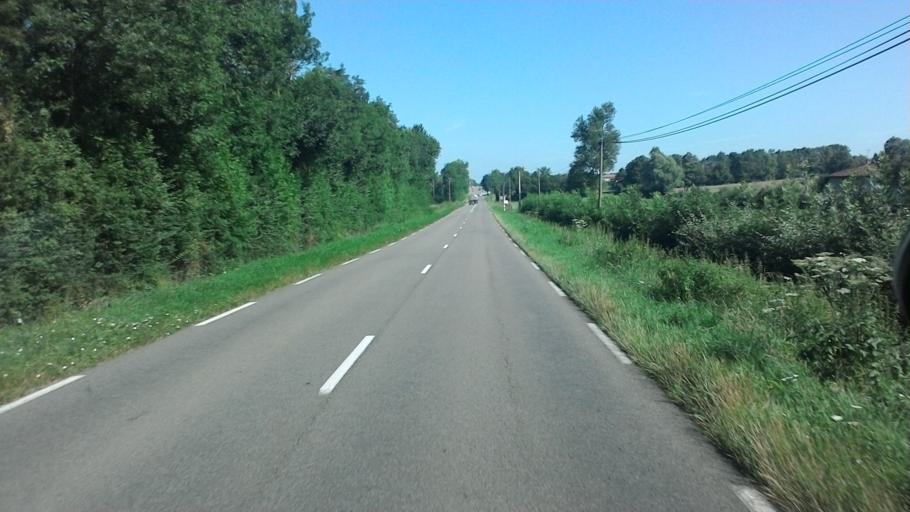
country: FR
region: Rhone-Alpes
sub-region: Departement de l'Ain
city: Saint-Trivier-de-Courtes
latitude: 46.4176
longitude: 5.1020
